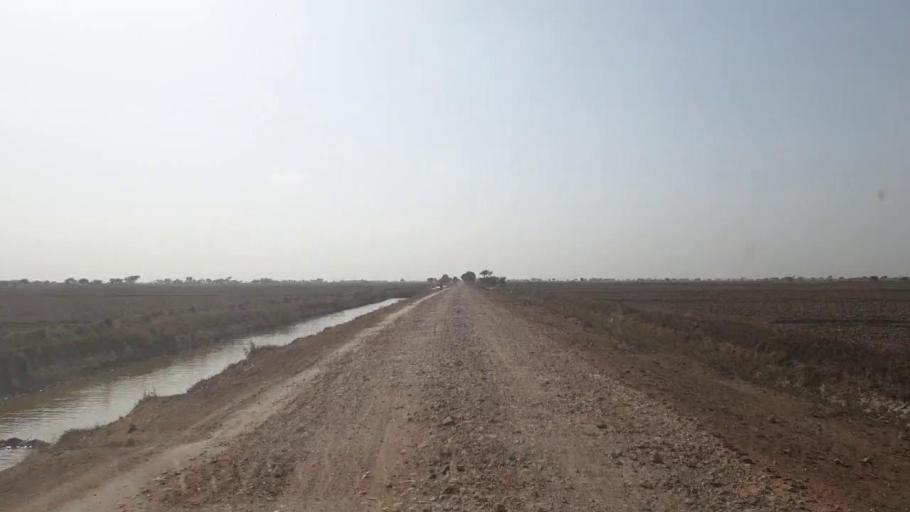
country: PK
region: Sindh
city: Kario
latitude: 24.5589
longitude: 68.5238
